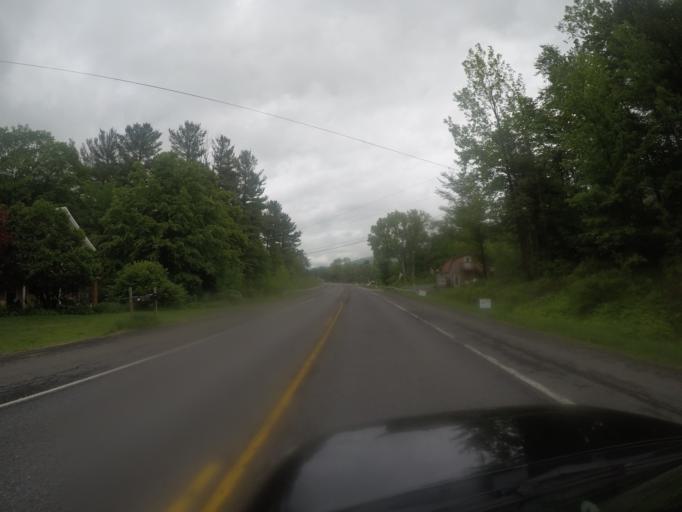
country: US
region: New York
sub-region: Ulster County
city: Shokan
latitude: 42.0379
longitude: -74.2779
